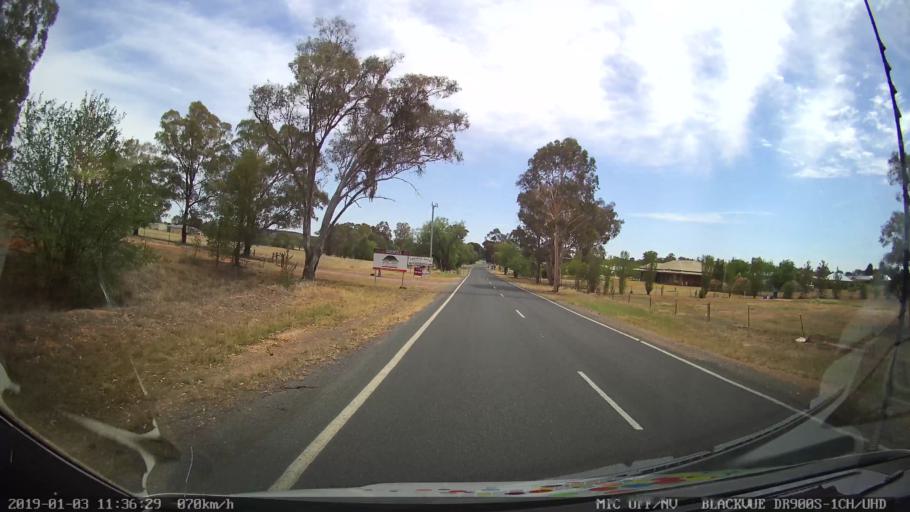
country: AU
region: New South Wales
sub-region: Weddin
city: Grenfell
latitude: -33.9102
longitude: 148.1598
